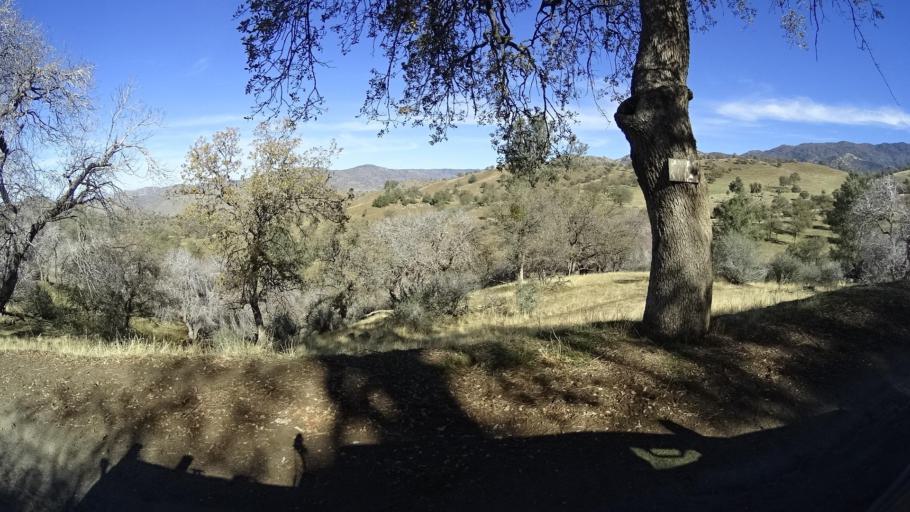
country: US
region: California
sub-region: Kern County
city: Bodfish
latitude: 35.4390
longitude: -118.7001
